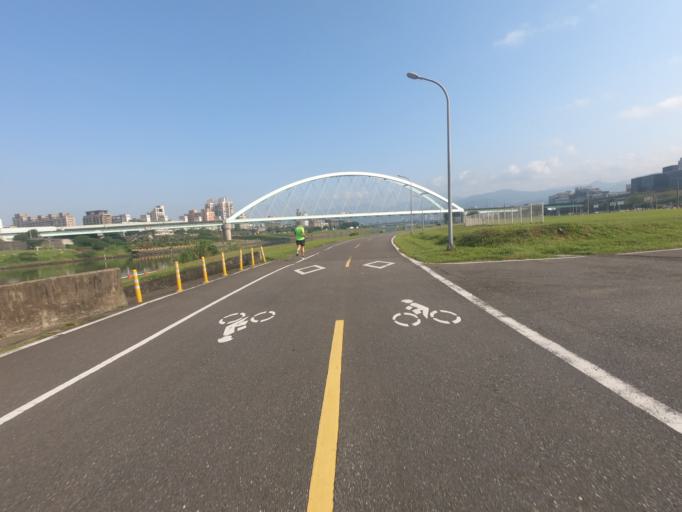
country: TW
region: Taipei
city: Taipei
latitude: 25.0536
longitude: 121.5727
